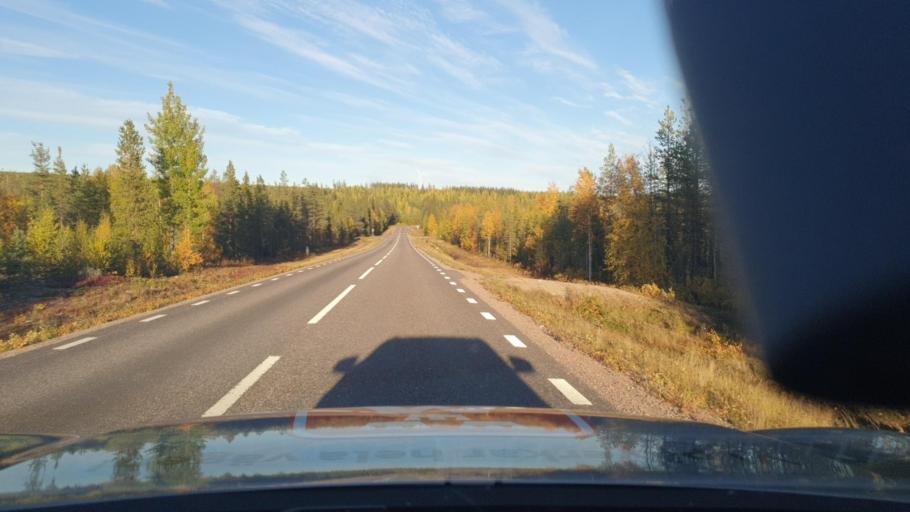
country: SE
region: Norrbotten
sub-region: Overkalix Kommun
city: OEverkalix
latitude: 67.0130
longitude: 21.9147
